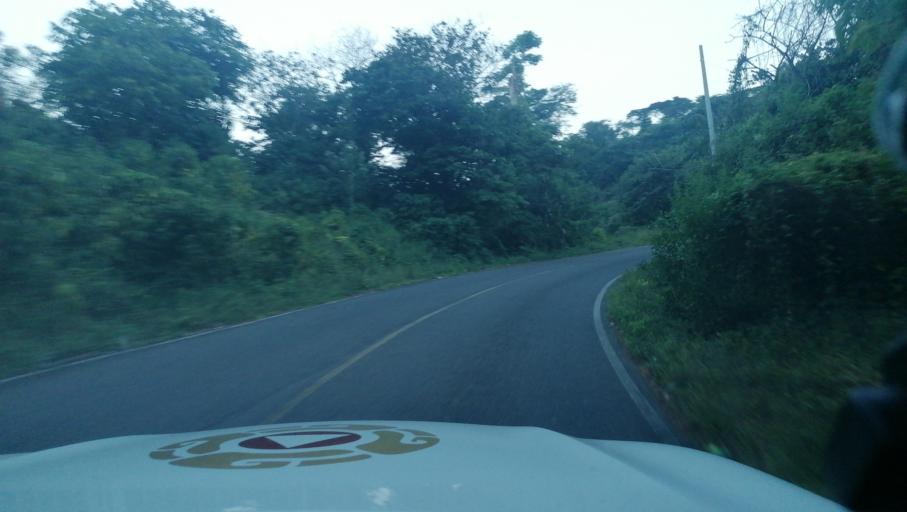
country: MX
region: Chiapas
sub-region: Cacahoatan
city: Benito Juarez
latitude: 15.0364
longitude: -92.2419
